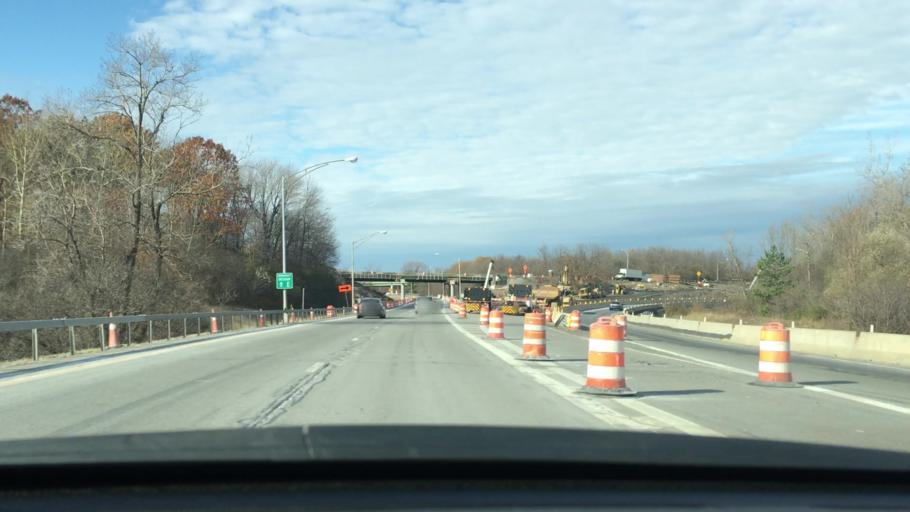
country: US
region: New York
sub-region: Monroe County
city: North Gates
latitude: 43.1579
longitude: -77.6766
